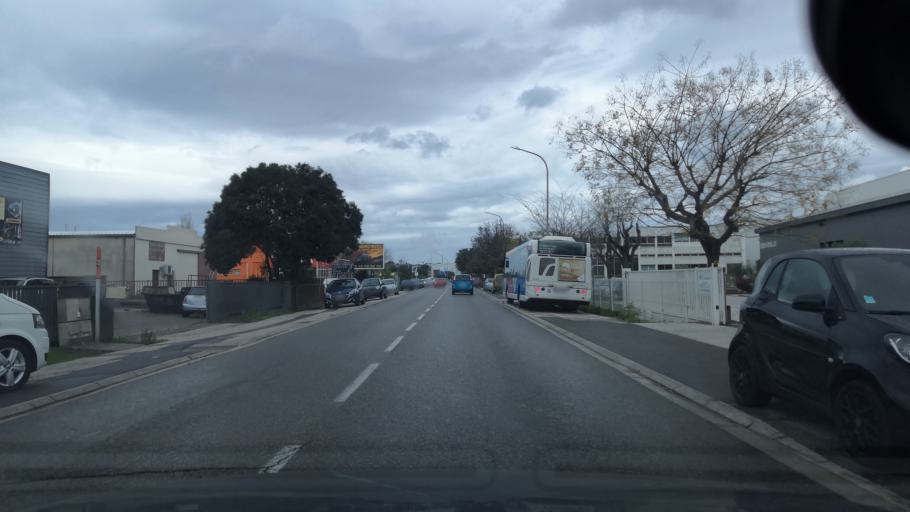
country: FR
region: Provence-Alpes-Cote d'Azur
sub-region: Departement des Bouches-du-Rhone
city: Gemenos
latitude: 43.2835
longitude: 5.6043
